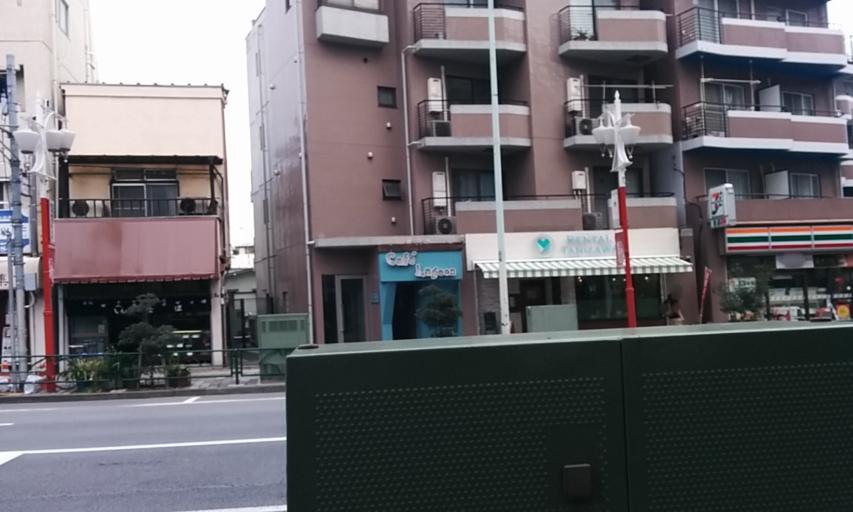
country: JP
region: Tokyo
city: Tokyo
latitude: 35.7104
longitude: 139.7125
